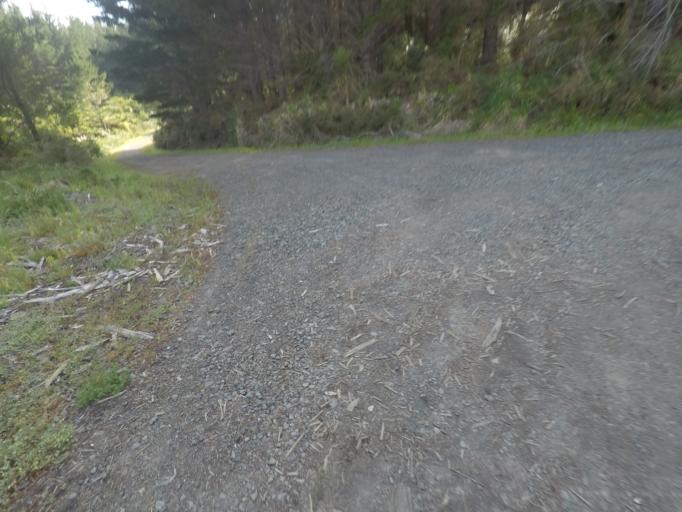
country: NZ
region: Auckland
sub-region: Auckland
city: Parakai
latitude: -36.7126
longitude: 174.5742
